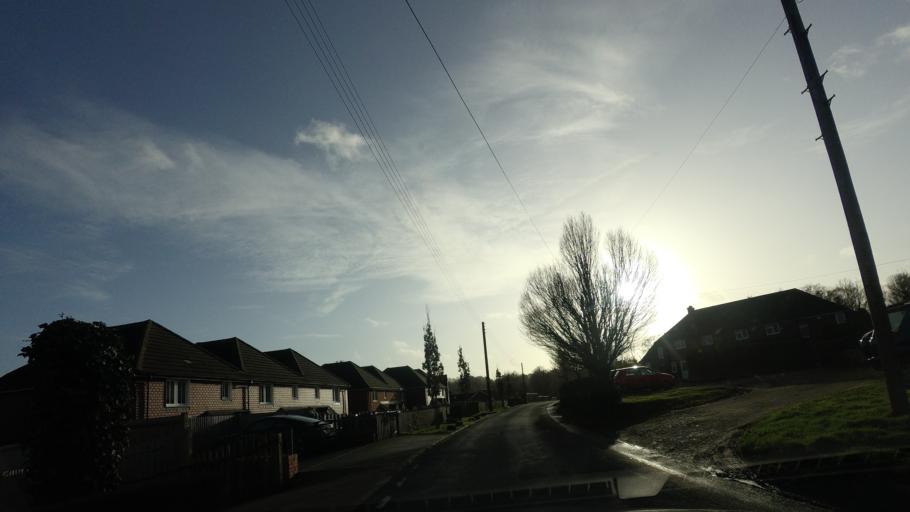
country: GB
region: England
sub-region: Kent
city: Borough Green
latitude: 51.2903
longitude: 0.2870
